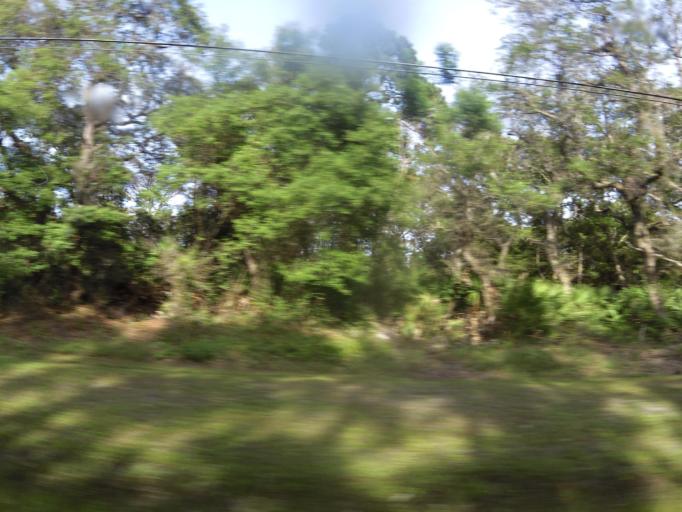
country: US
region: Florida
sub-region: Duval County
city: Atlantic Beach
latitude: 30.4755
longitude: -81.4700
